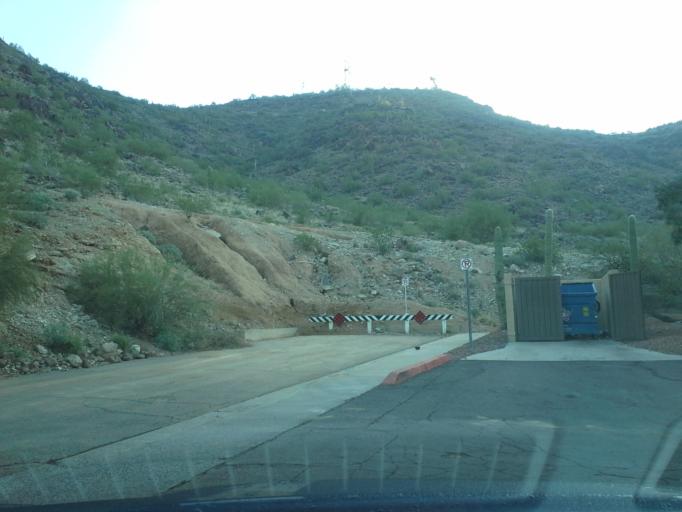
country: US
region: Arizona
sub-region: Maricopa County
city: Glendale
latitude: 33.5929
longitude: -112.0937
